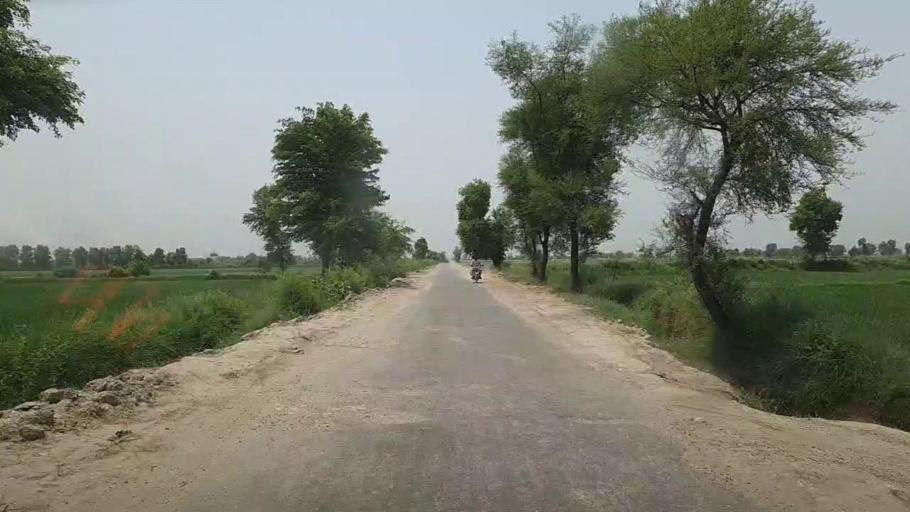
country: PK
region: Sindh
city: Sita Road
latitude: 27.0720
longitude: 67.9066
